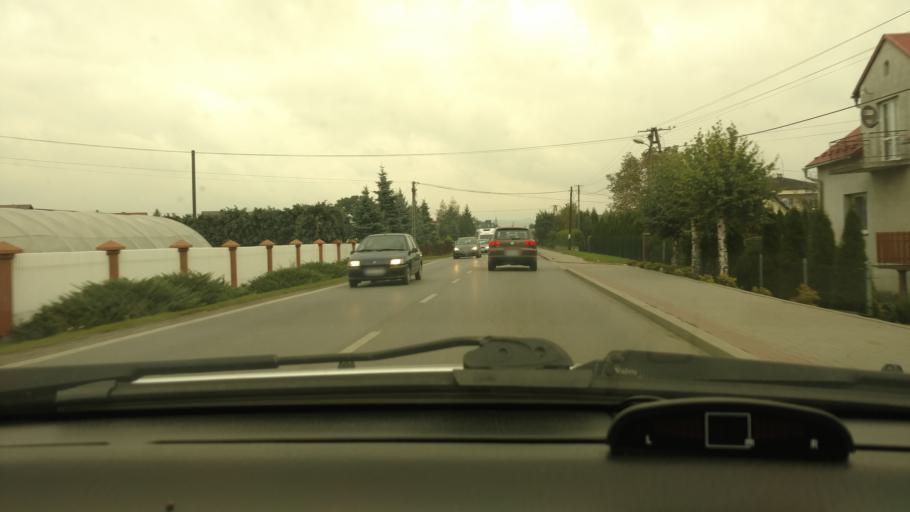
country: PL
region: Lesser Poland Voivodeship
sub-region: Powiat nowosadecki
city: Chelmiec
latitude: 49.6160
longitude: 20.6644
